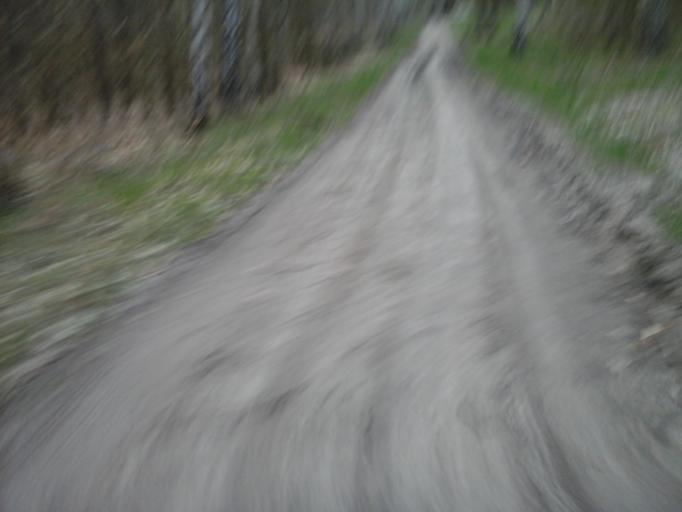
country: PL
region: West Pomeranian Voivodeship
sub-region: Powiat choszczenski
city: Bierzwnik
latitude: 53.0354
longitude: 15.6478
